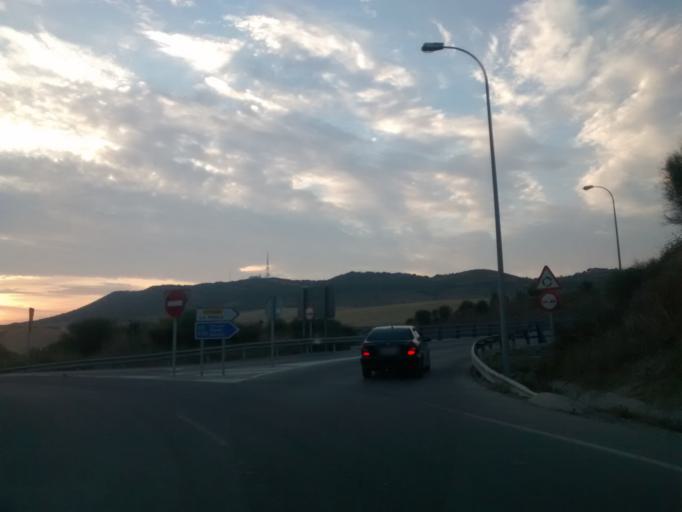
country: ES
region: Andalusia
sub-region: Provincia de Cadiz
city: Vejer de la Frontera
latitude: 36.2537
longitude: -5.9831
